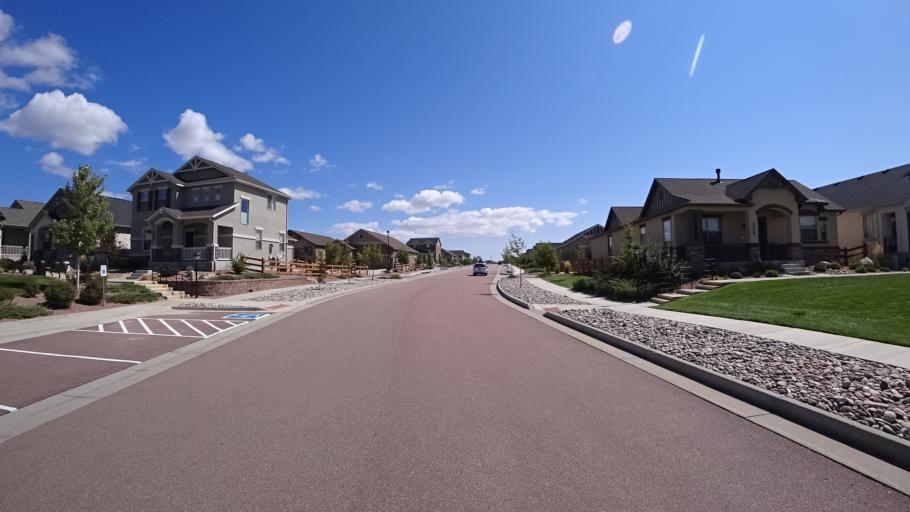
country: US
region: Colorado
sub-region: El Paso County
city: Cimarron Hills
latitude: 38.9276
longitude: -104.6886
